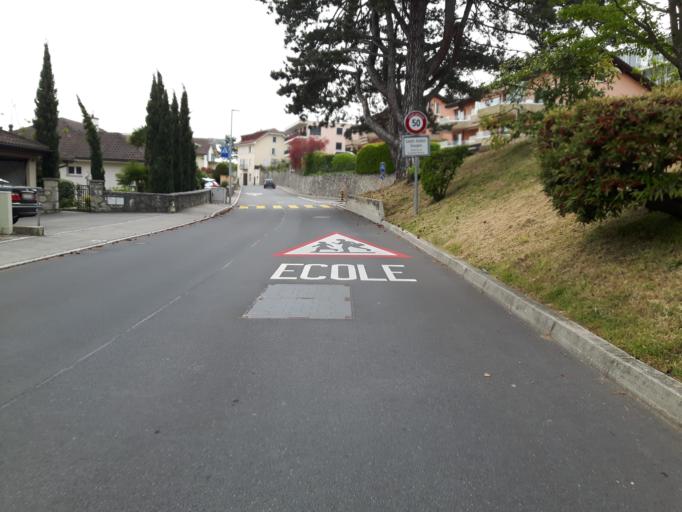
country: CH
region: Neuchatel
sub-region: Boudry District
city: Gorgier
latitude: 46.8981
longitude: 6.7767
